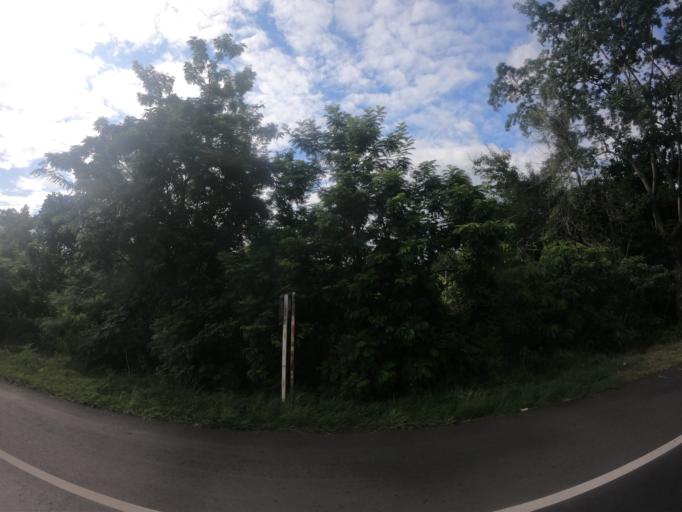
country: TH
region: Surin
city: Prasat
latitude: 14.6187
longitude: 103.3627
